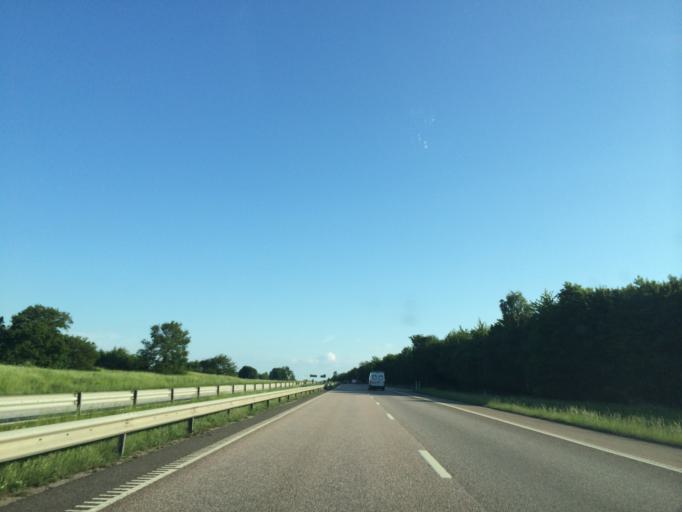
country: SE
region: Skane
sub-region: Helsingborg
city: Gantofta
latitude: 56.0155
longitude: 12.7808
